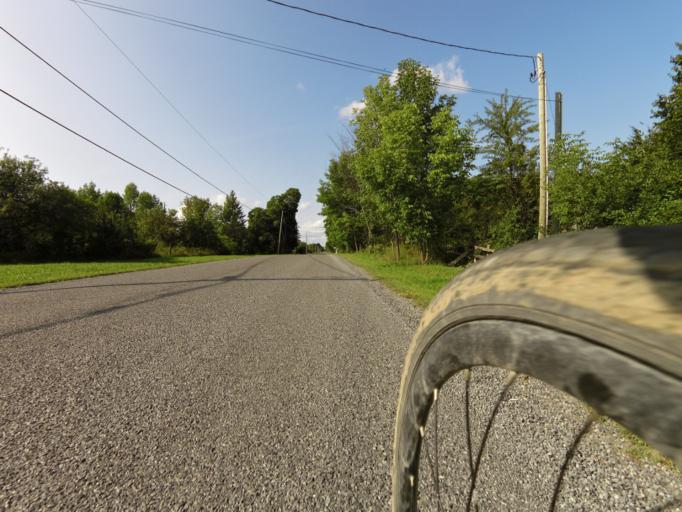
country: CA
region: Ontario
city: Kingston
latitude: 44.3843
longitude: -76.5956
